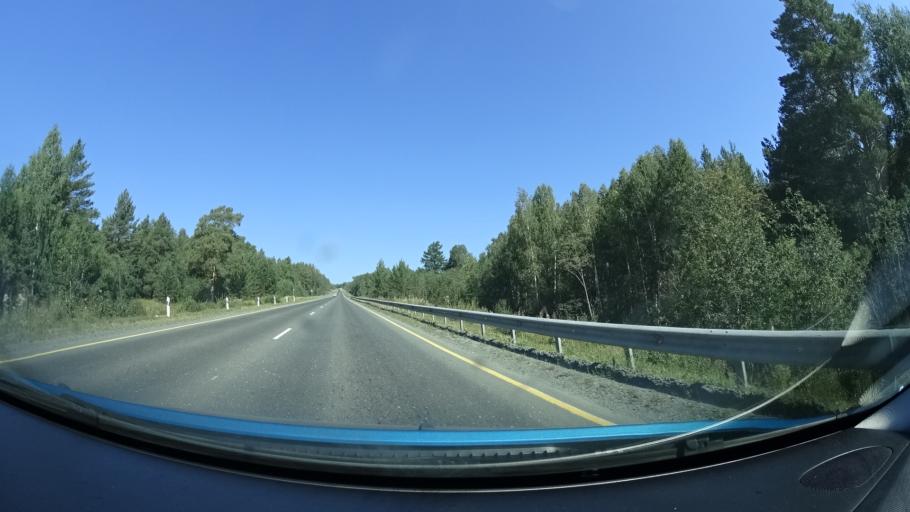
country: RU
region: Bashkortostan
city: Abzakovo
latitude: 53.8752
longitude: 58.5346
